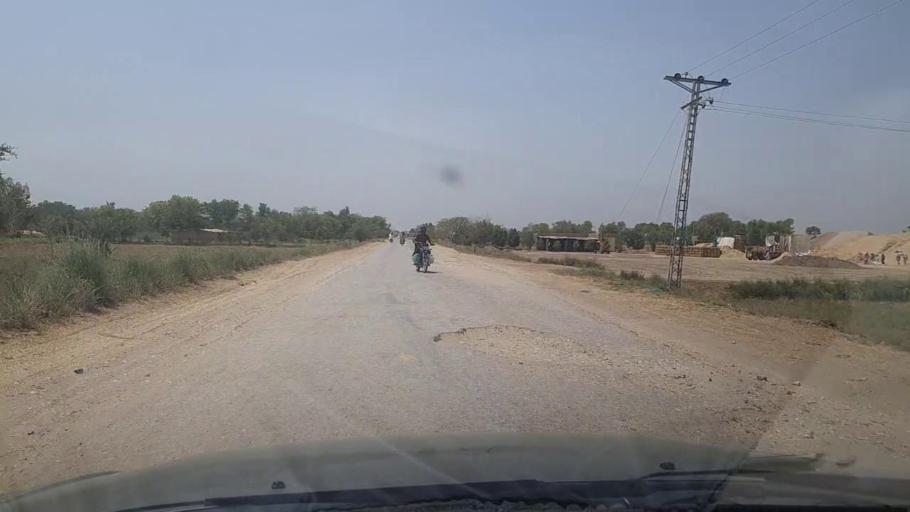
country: PK
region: Sindh
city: Karaundi
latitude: 26.8804
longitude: 68.3089
